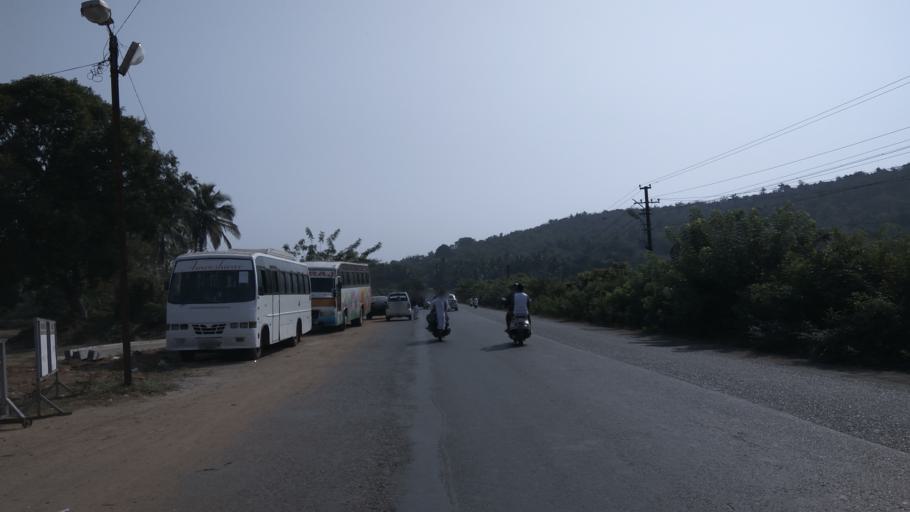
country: IN
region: Goa
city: Calangute
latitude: 15.5416
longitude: 73.7710
